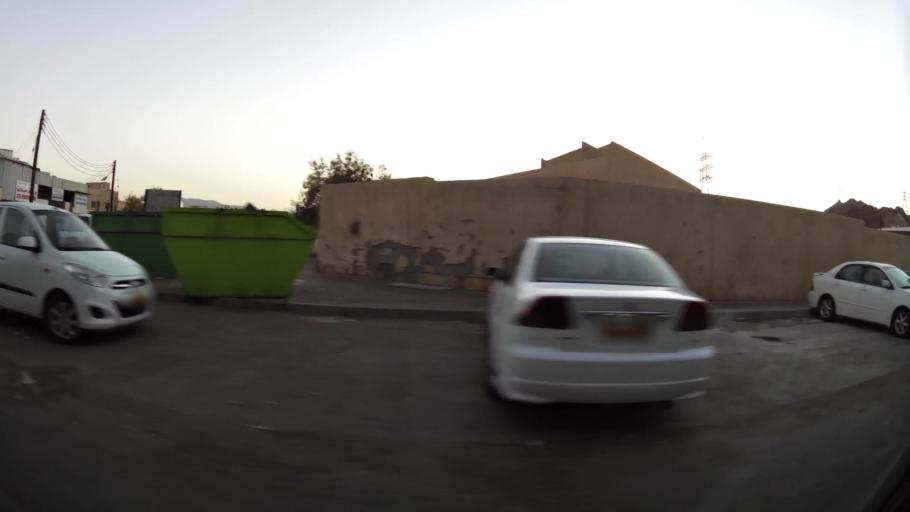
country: OM
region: Muhafazat Masqat
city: Muscat
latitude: 23.5930
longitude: 58.5643
